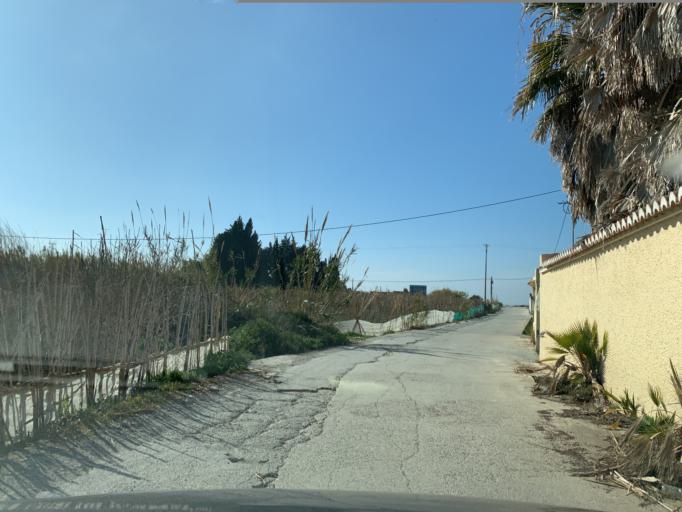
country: ES
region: Andalusia
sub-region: Provincia de Granada
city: Salobrena
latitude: 36.7253
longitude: -3.5576
